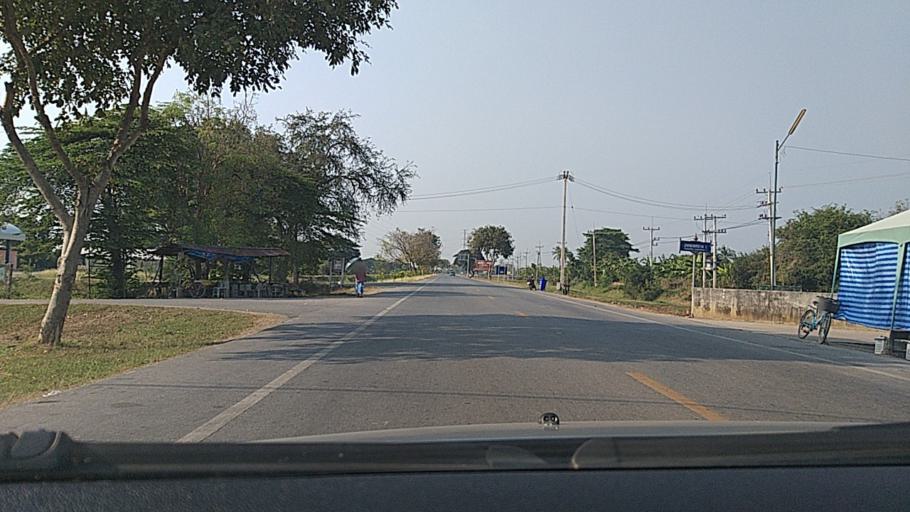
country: TH
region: Ang Thong
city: Chaiyo
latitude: 14.7190
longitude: 100.4323
